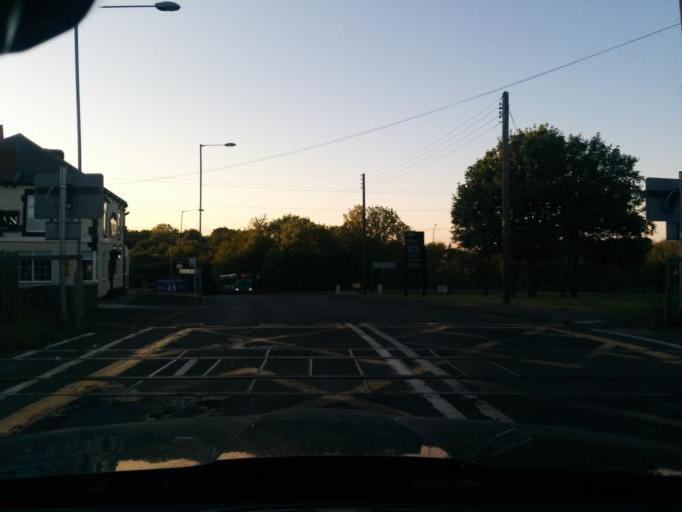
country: GB
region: England
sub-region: Northumberland
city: Choppington
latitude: 55.1450
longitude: -1.5997
